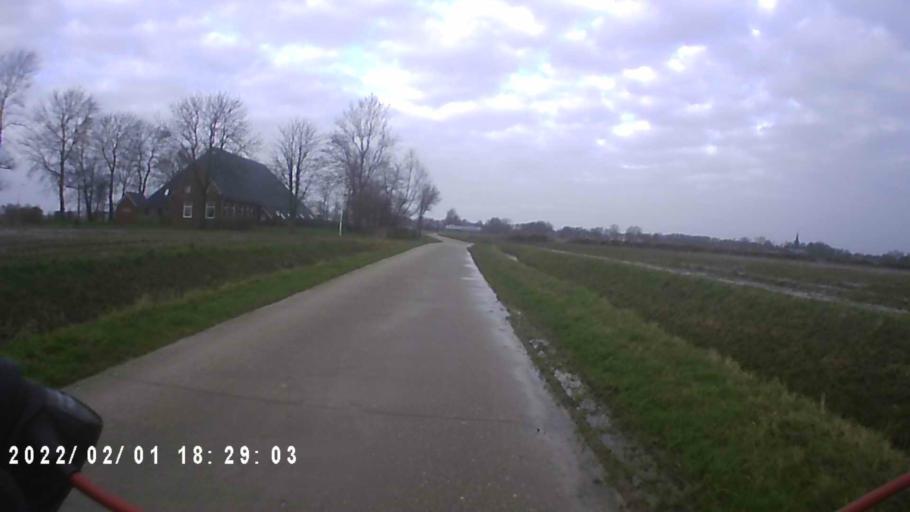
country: NL
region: Groningen
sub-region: Gemeente De Marne
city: Ulrum
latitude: 53.3539
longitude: 6.3201
